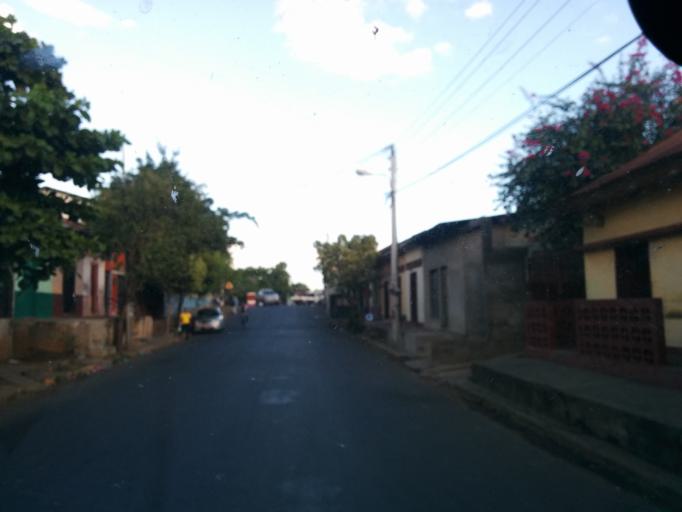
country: NI
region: Leon
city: Leon
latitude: 12.4267
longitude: -86.8788
